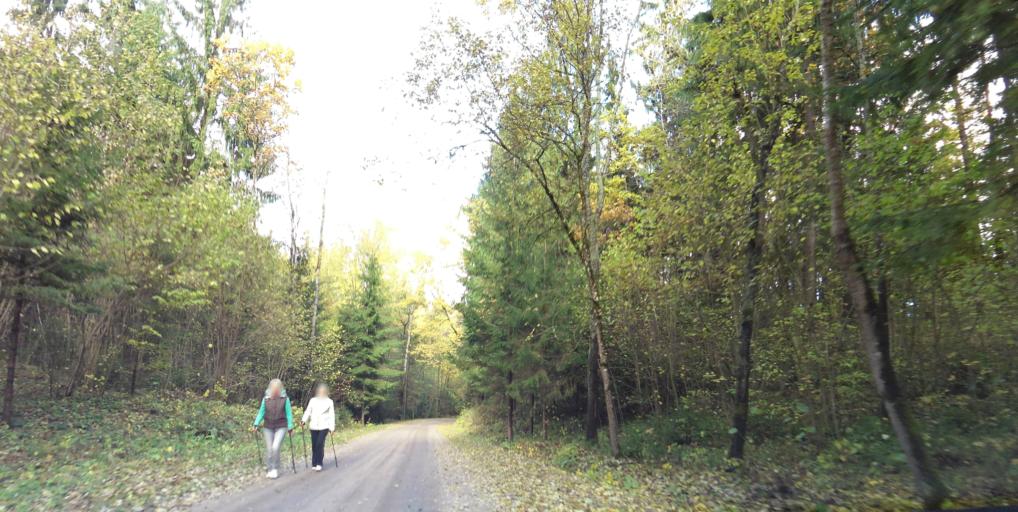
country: LT
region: Vilnius County
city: Vilkpede
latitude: 54.6534
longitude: 25.2562
